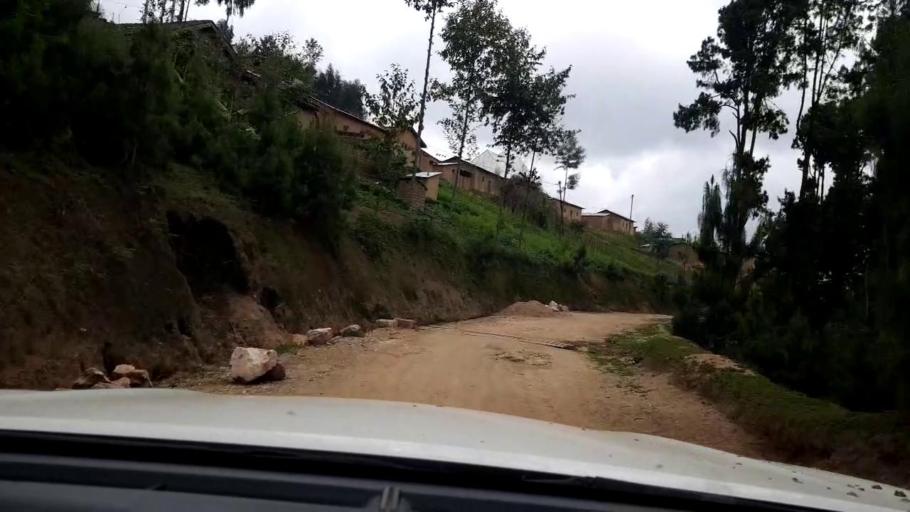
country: RW
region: Western Province
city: Kibuye
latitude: -1.8931
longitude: 29.5280
